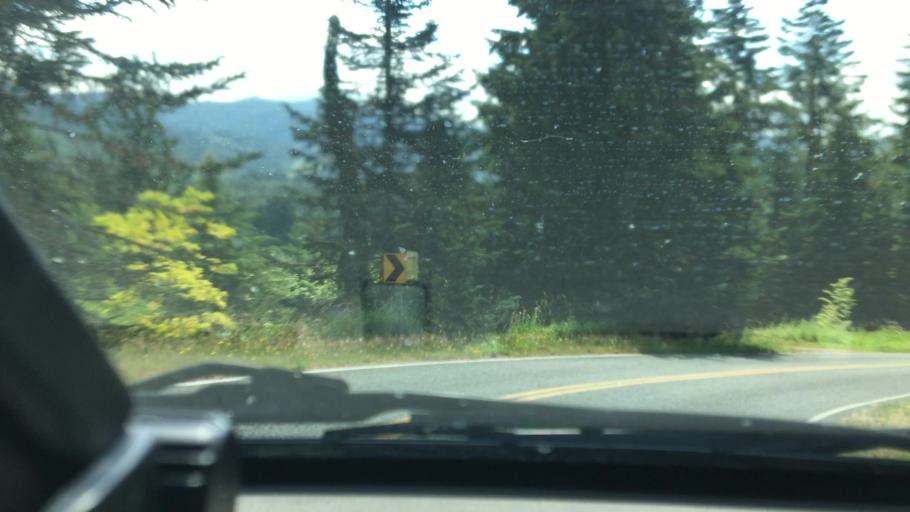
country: US
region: Washington
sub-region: Whatcom County
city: Geneva
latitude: 48.7630
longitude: -122.3680
